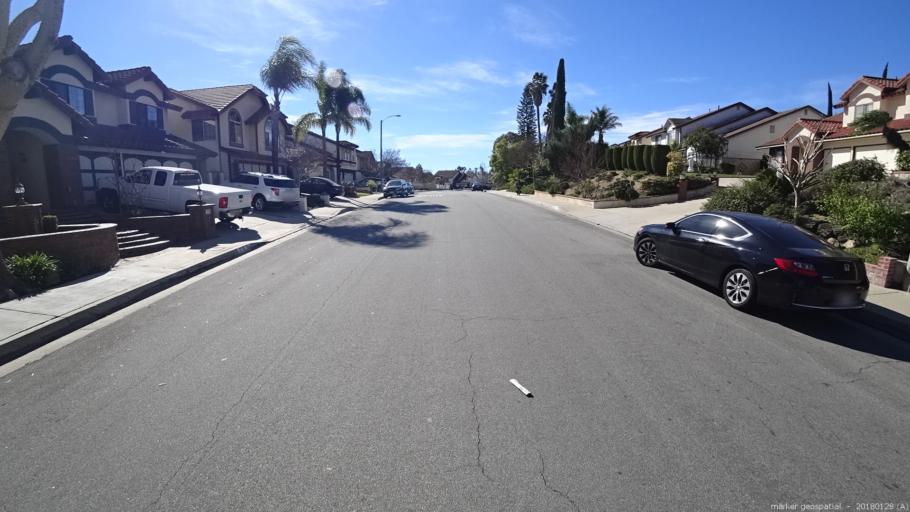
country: US
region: California
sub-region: Los Angeles County
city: Diamond Bar
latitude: 34.0016
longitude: -117.7942
